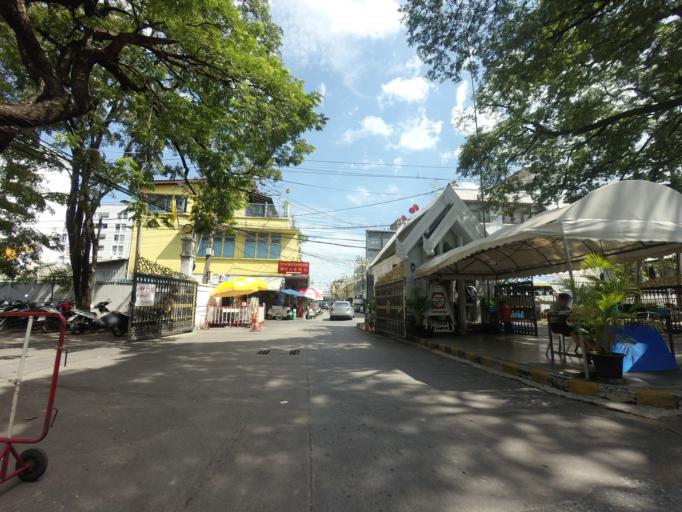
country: TH
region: Bangkok
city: Khlong Toei
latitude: 13.7233
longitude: 100.5554
